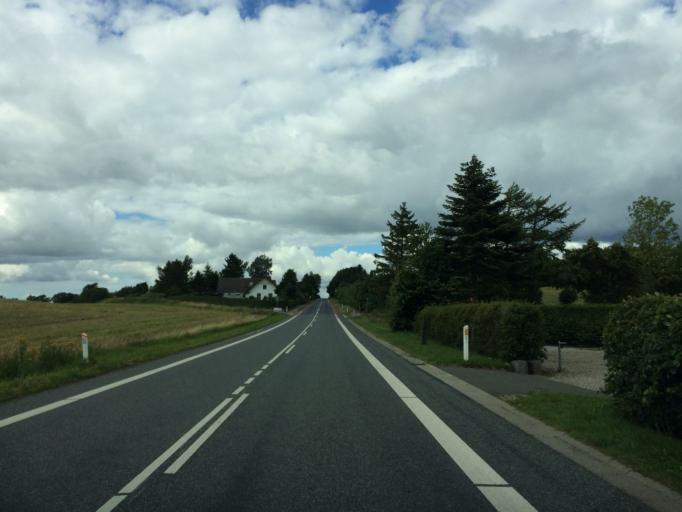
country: DK
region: South Denmark
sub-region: Assens Kommune
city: Harby
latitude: 55.1816
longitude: 10.1540
